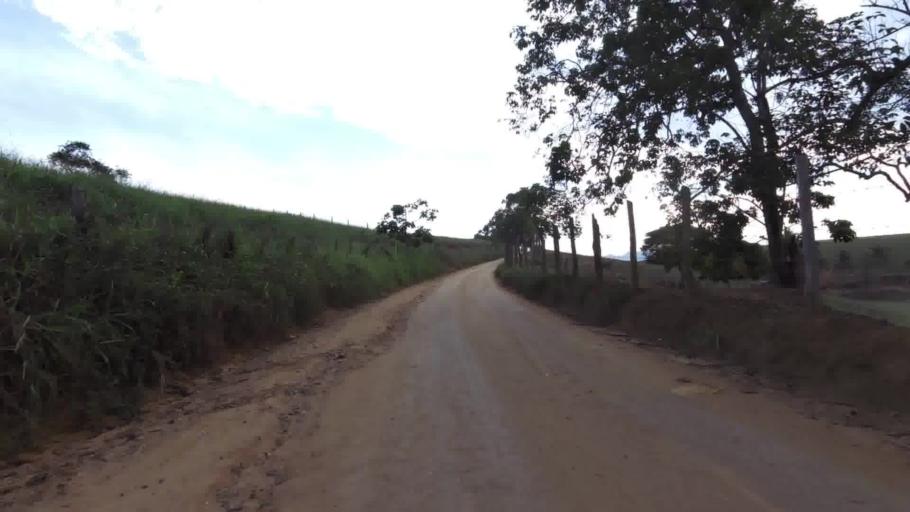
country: BR
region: Espirito Santo
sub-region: Piuma
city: Piuma
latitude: -20.8346
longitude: -40.7437
